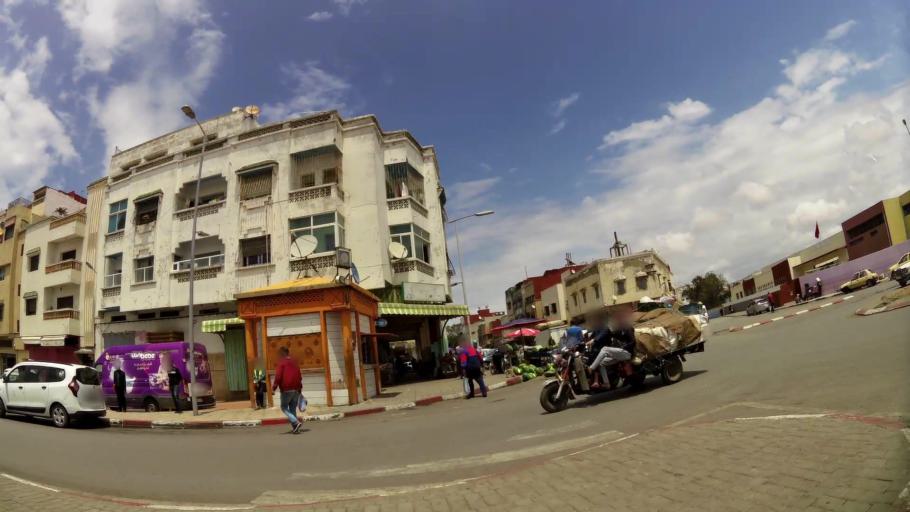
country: MA
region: Rabat-Sale-Zemmour-Zaer
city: Sale
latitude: 34.0418
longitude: -6.8209
